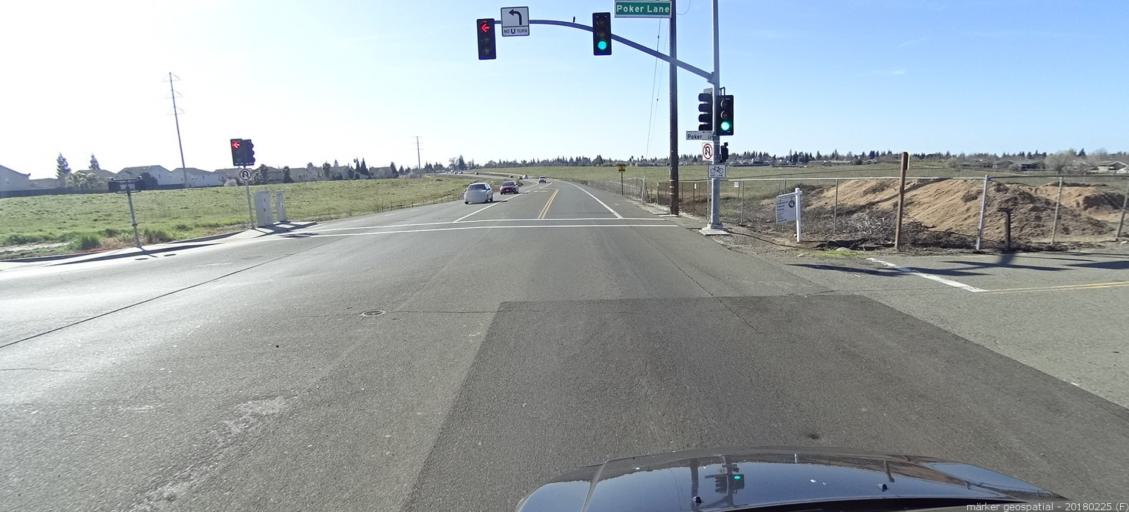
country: US
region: California
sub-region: Sacramento County
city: Antelope
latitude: 38.7106
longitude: -121.3475
